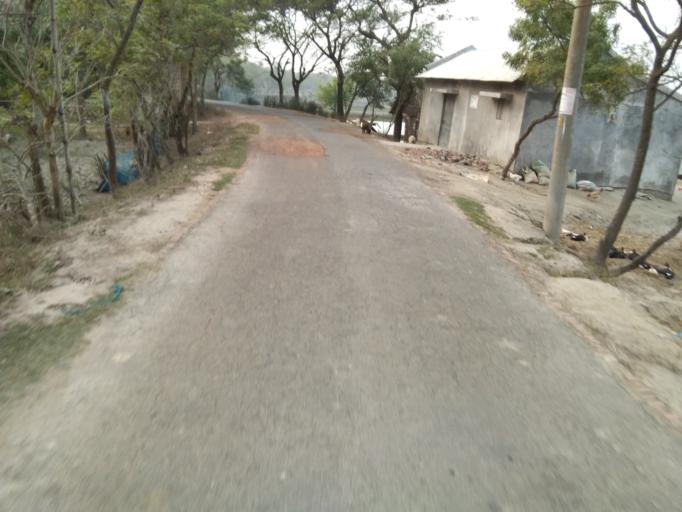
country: BD
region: Khulna
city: Satkhira
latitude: 22.5781
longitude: 89.0724
